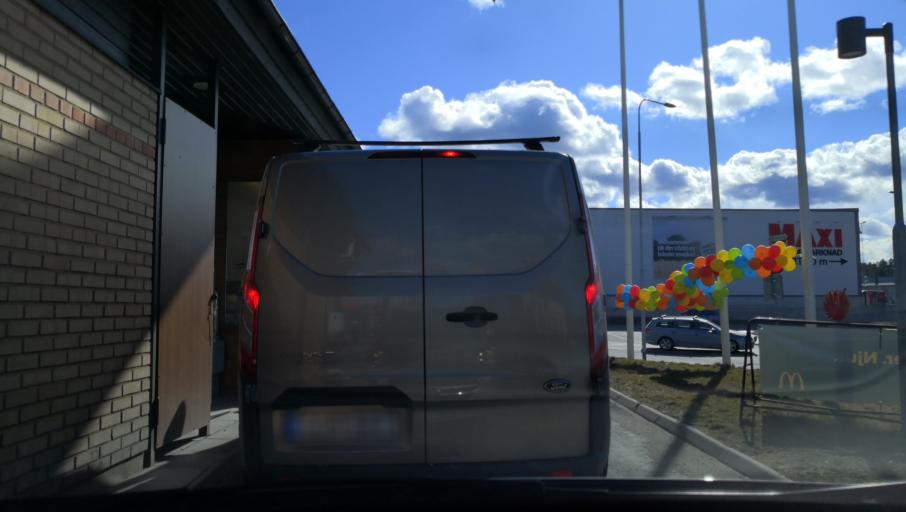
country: SE
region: Stockholm
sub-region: Varmdo Kommun
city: Mortnas
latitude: 59.3129
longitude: 18.4271
